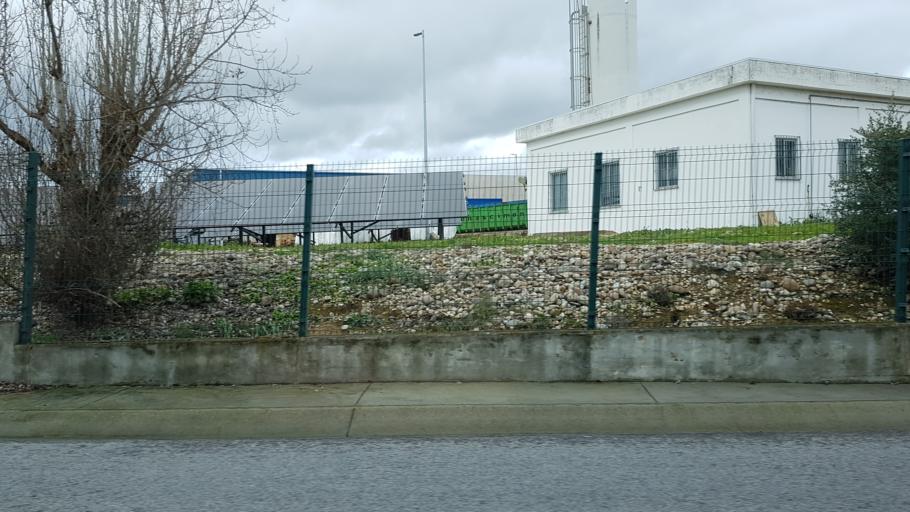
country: PT
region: Lisbon
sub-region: Alenquer
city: Carregado
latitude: 39.0318
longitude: -8.9741
